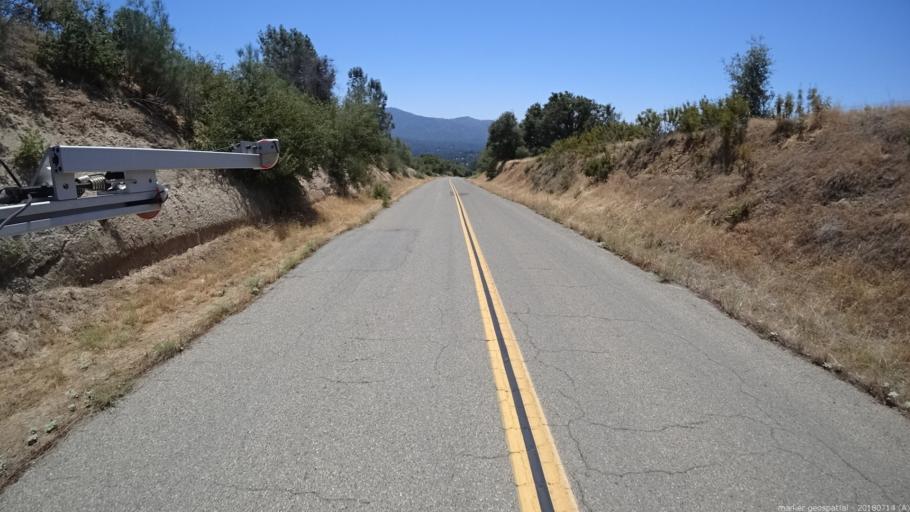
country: US
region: California
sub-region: Madera County
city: Ahwahnee
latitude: 37.3850
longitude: -119.7169
